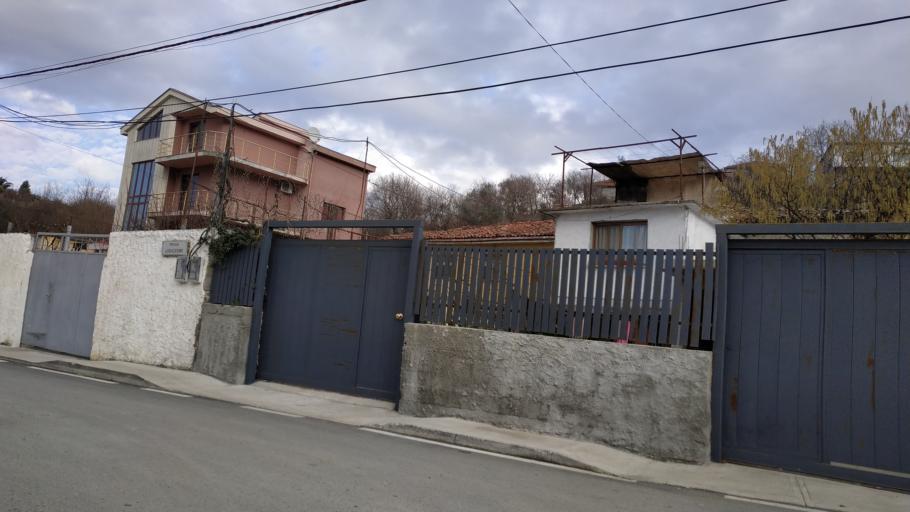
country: AL
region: Shkoder
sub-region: Rrethi i Shkodres
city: Shkoder
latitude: 42.0545
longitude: 19.5034
